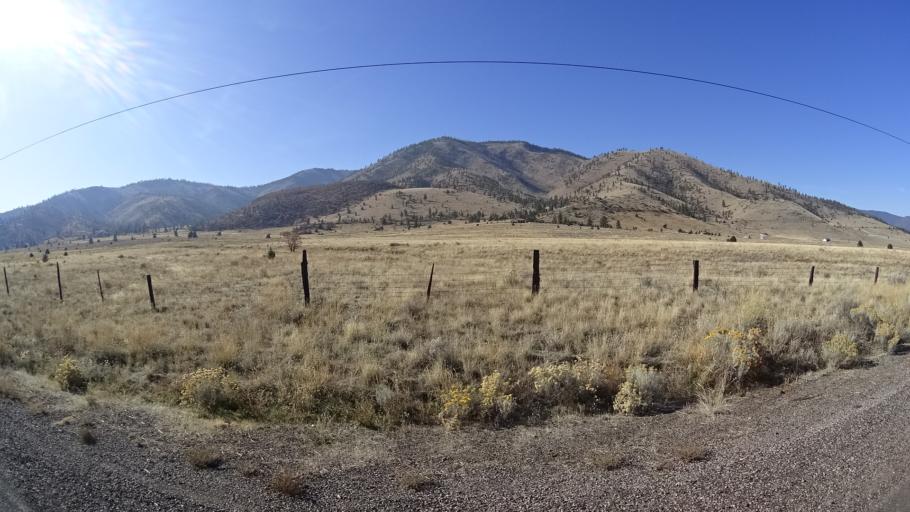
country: US
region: California
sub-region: Siskiyou County
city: Weed
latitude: 41.4802
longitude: -122.4917
